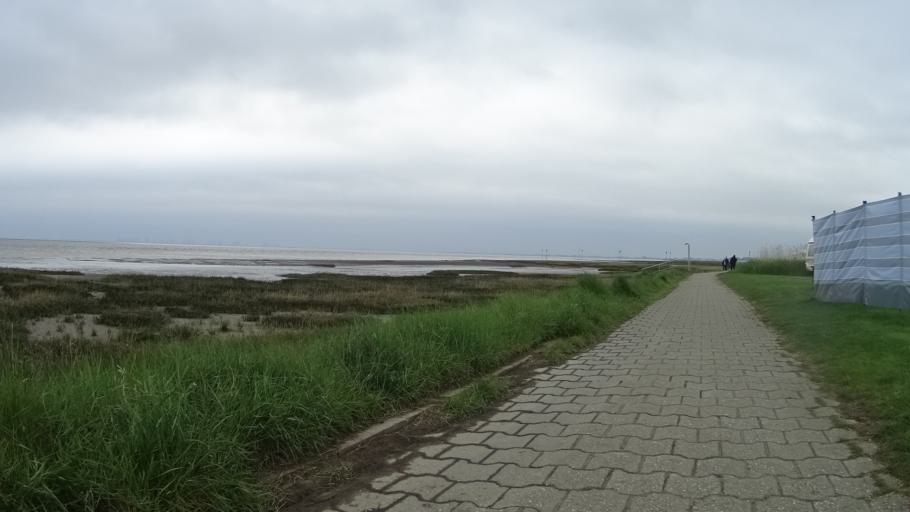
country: DE
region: Lower Saxony
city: Butjadingen
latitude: 53.5971
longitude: 8.3591
